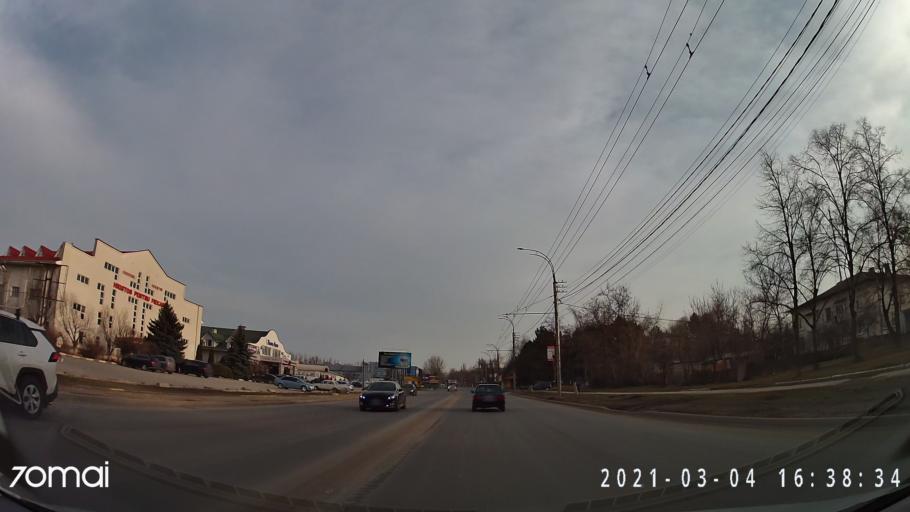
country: MD
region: Balti
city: Balti
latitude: 47.7802
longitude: 27.8916
